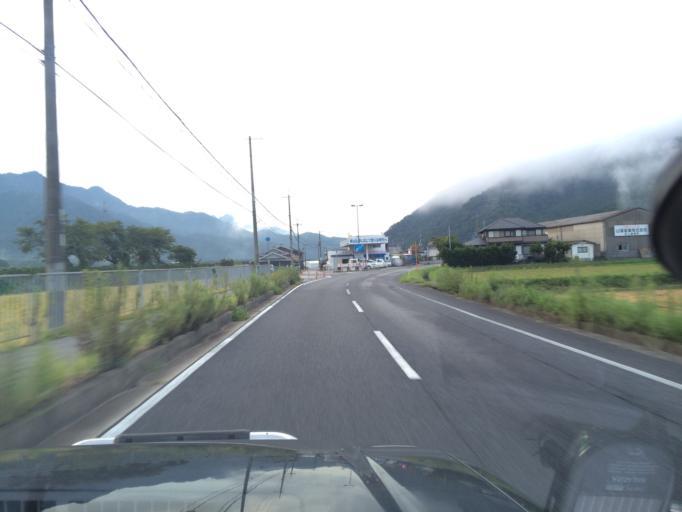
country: JP
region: Hyogo
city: Nishiwaki
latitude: 35.1187
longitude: 135.0035
